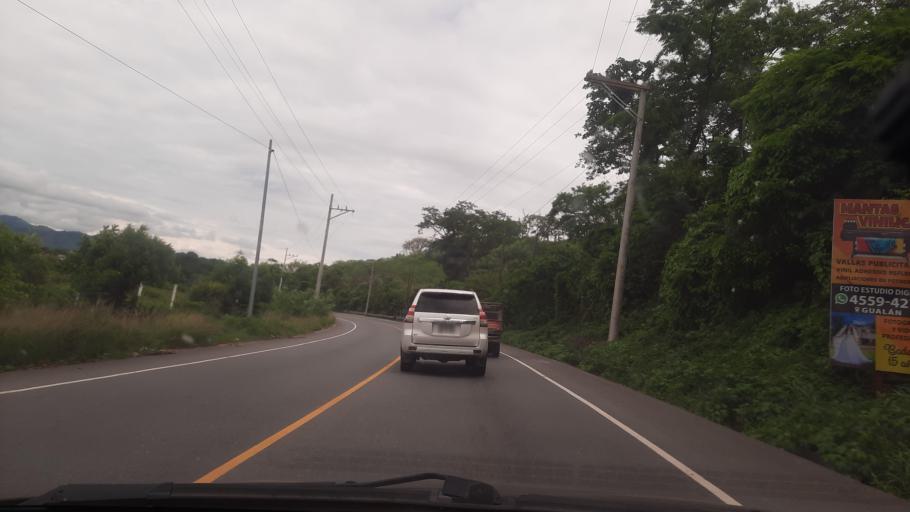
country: GT
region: Zacapa
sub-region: Municipio de Zacapa
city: Gualan
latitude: 15.1352
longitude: -89.3427
